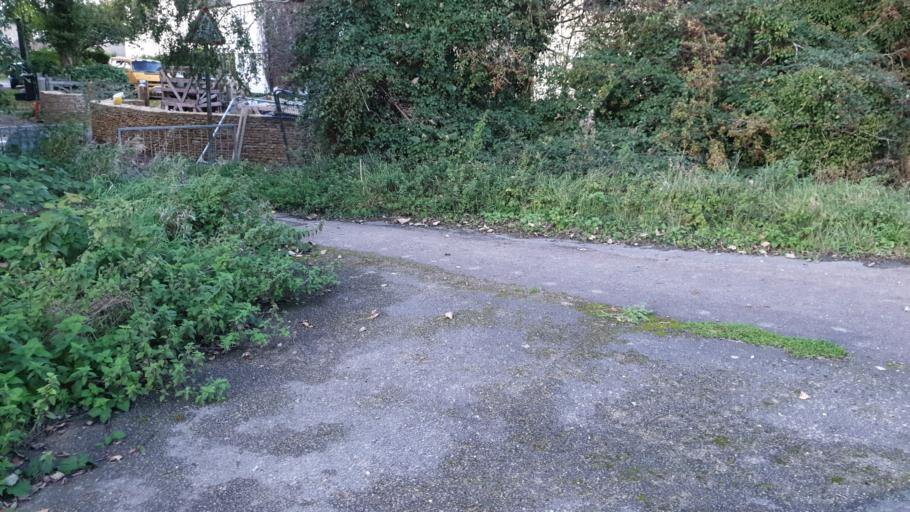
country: GB
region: England
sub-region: Wiltshire
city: Minety
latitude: 51.6509
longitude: -1.9713
